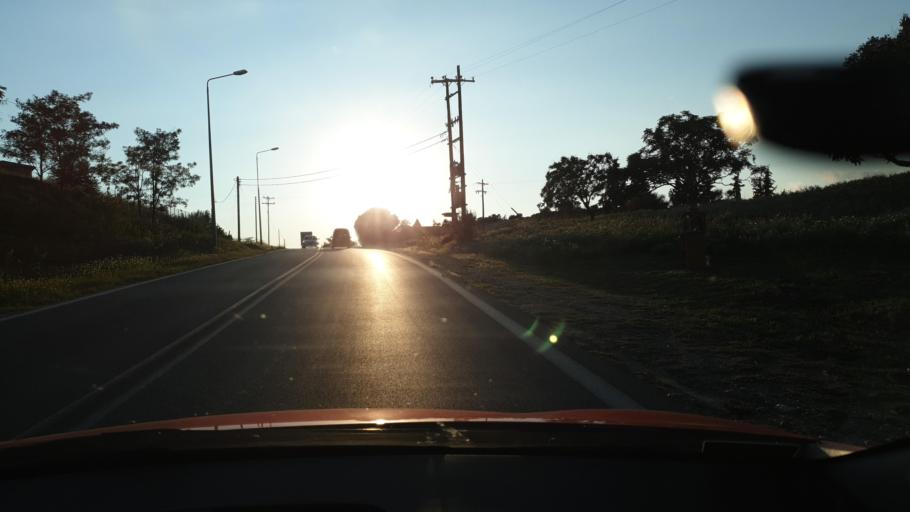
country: GR
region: Central Macedonia
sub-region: Nomos Chalkidikis
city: Arnaia
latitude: 40.5052
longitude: 23.4739
